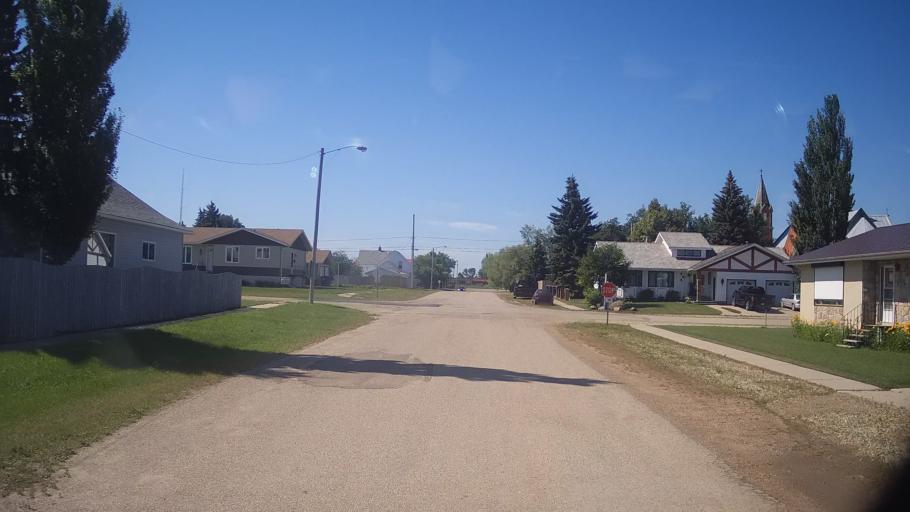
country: CA
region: Saskatchewan
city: Saskatoon
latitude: 51.8958
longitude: -106.0563
